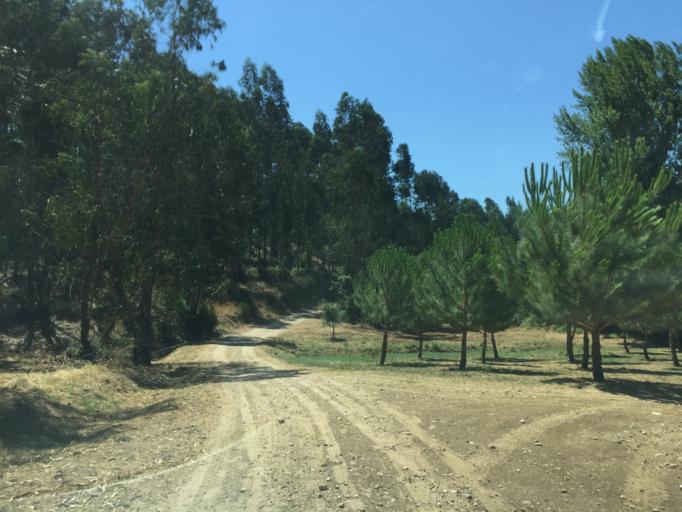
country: PT
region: Santarem
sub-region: Tomar
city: Tomar
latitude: 39.6061
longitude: -8.3589
